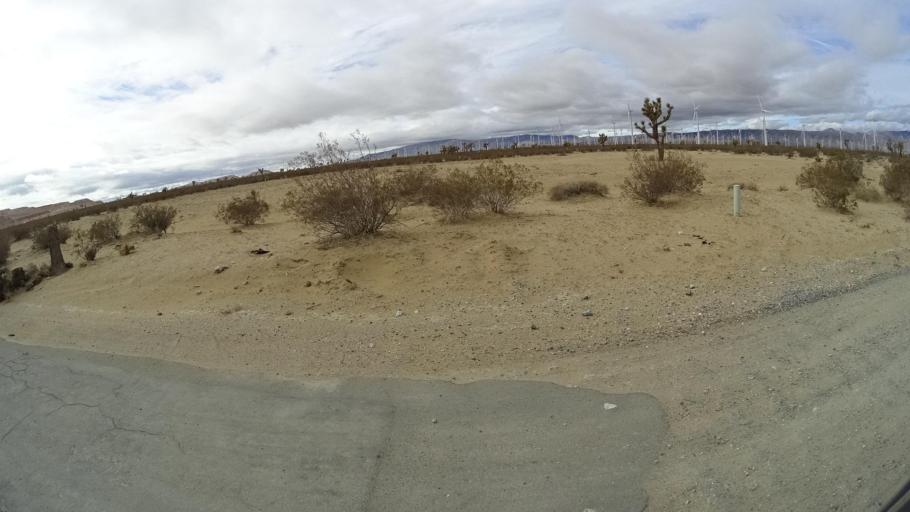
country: US
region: California
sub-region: Kern County
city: Mojave
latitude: 35.0072
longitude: -118.1858
